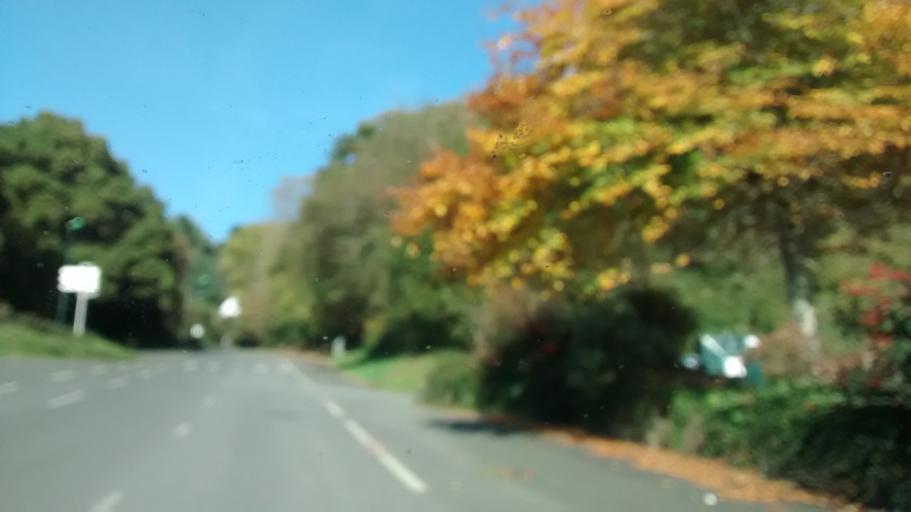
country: FR
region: Brittany
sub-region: Departement des Cotes-d'Armor
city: Trebeurden
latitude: 48.7617
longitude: -3.5653
